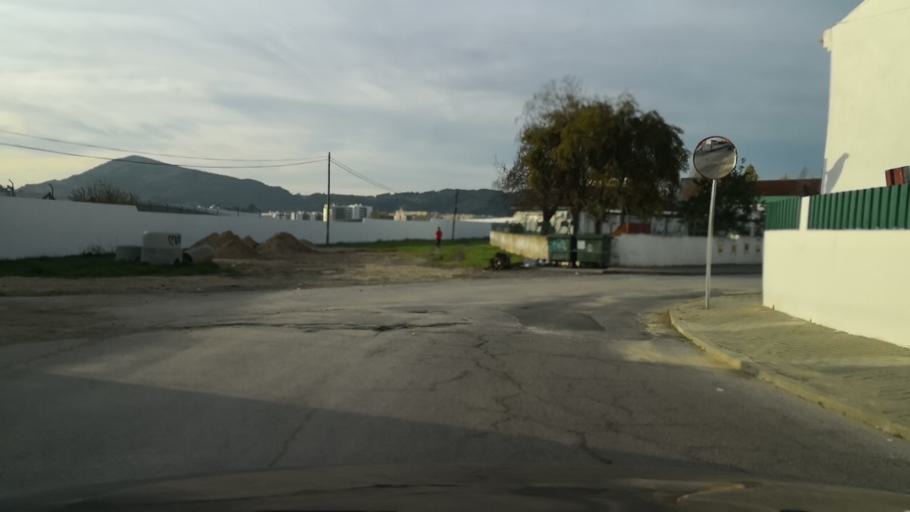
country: PT
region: Setubal
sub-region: Setubal
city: Setubal
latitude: 38.5335
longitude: -8.8799
